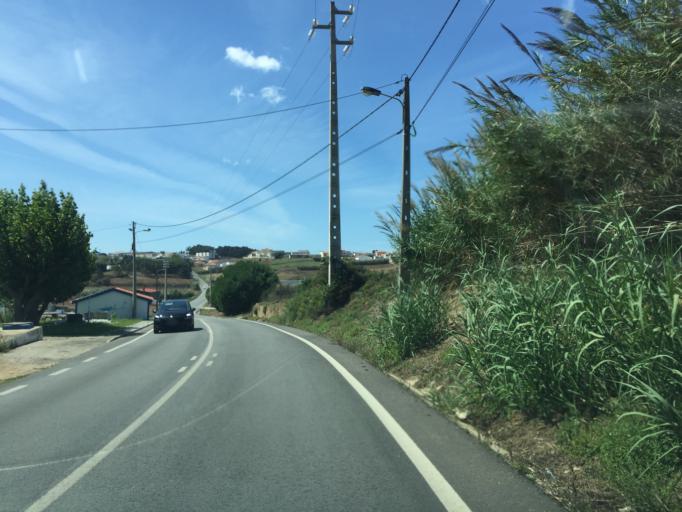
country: PT
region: Lisbon
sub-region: Lourinha
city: Lourinha
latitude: 39.2642
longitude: -9.3130
